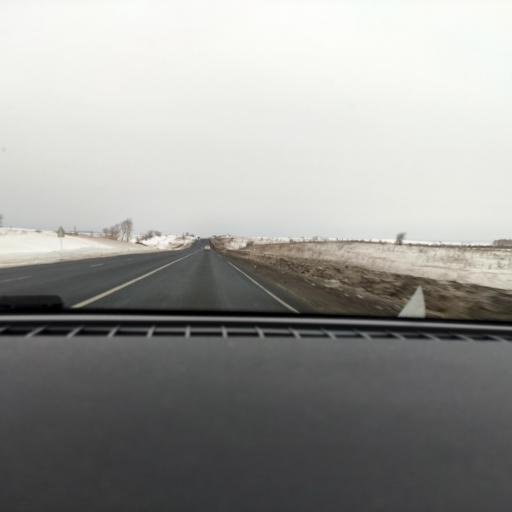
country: RU
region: Samara
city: Novosemeykino
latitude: 53.4008
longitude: 50.4054
